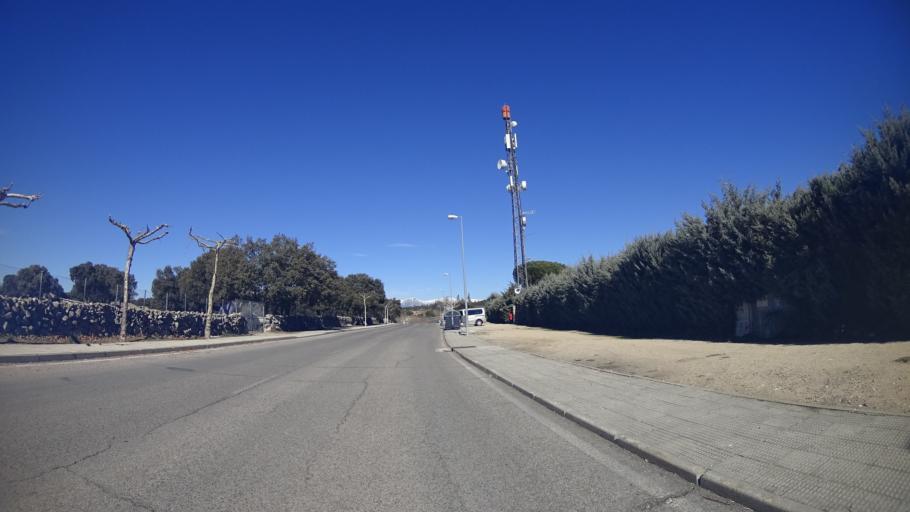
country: ES
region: Madrid
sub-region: Provincia de Madrid
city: Colmenarejo
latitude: 40.5519
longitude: -4.0136
